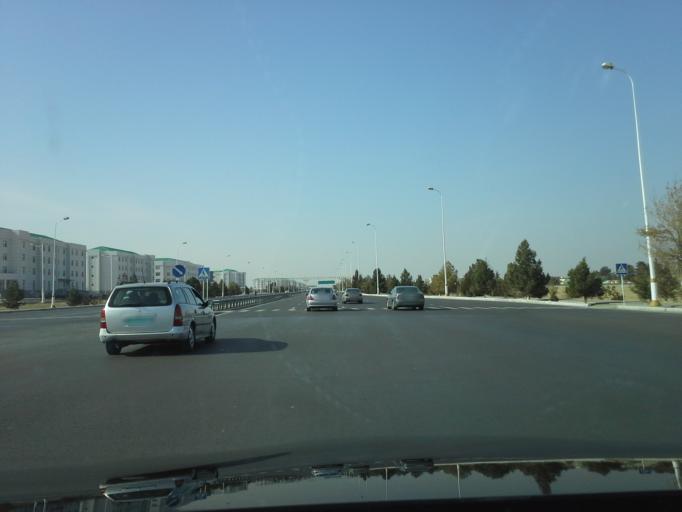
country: TM
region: Ahal
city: Ashgabat
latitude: 37.9816
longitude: 58.3358
